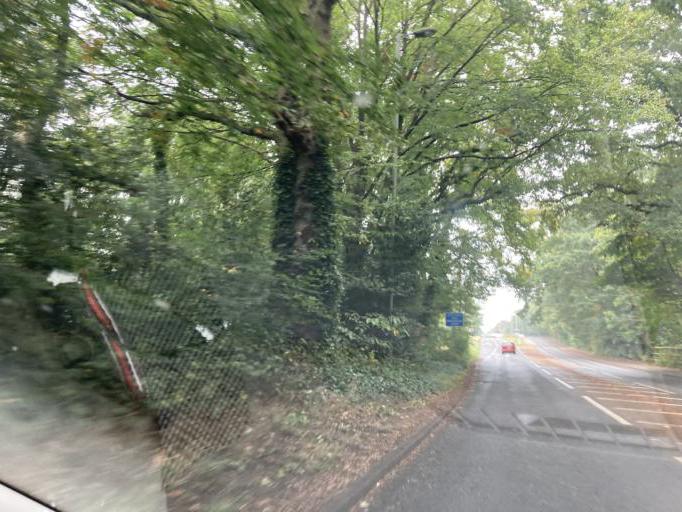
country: GB
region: England
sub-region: Surrey
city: Camberley
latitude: 51.3450
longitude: -0.7260
